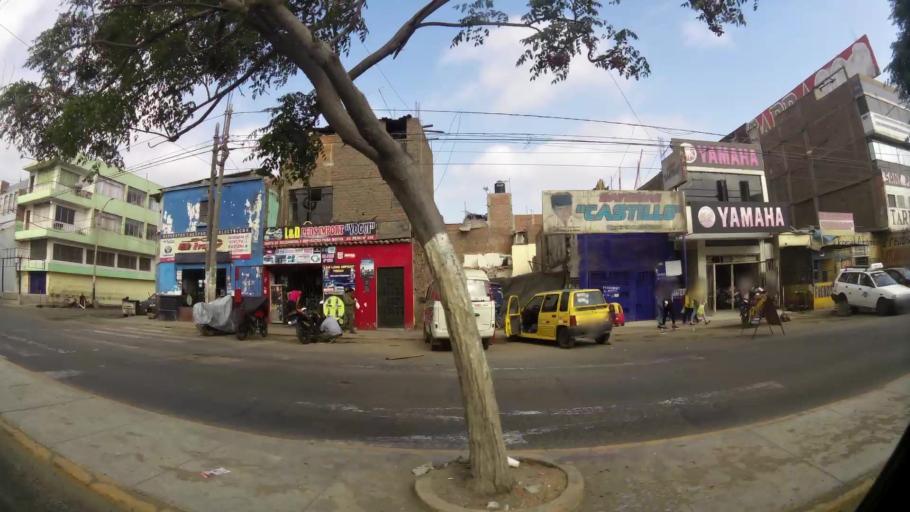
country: PE
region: La Libertad
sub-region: Provincia de Trujillo
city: Trujillo
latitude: -8.1019
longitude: -79.0164
